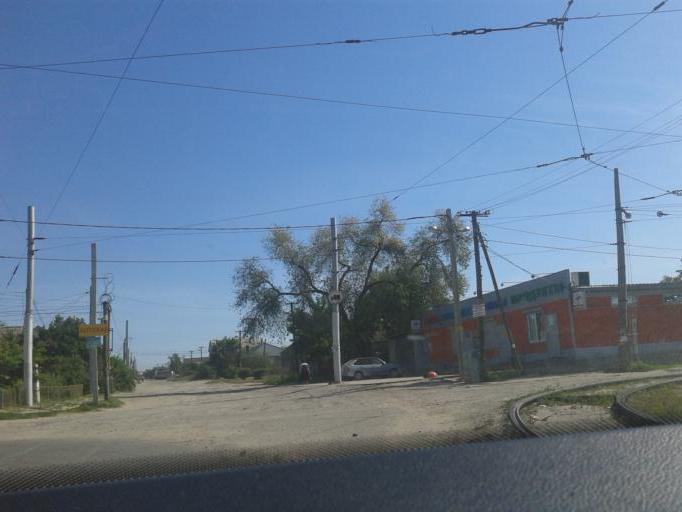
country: RU
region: Volgograd
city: Volgograd
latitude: 48.6926
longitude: 44.4551
